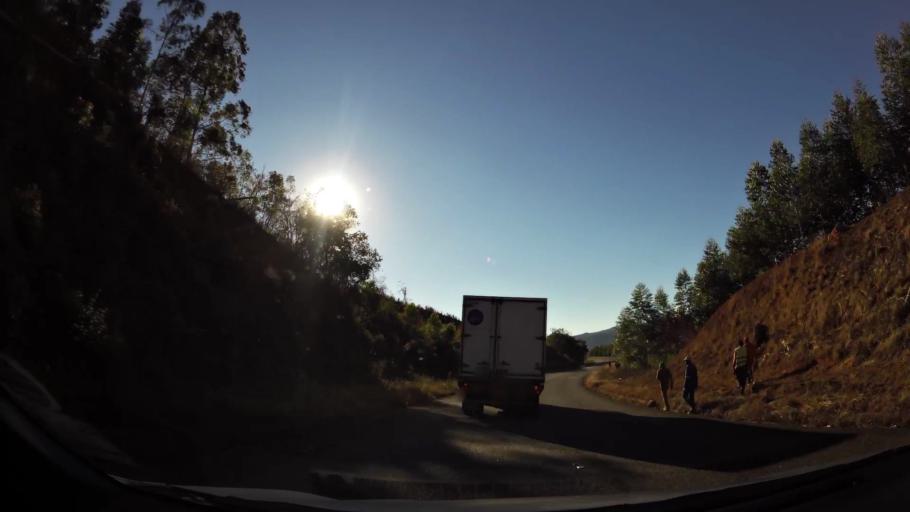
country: ZA
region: Limpopo
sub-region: Mopani District Municipality
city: Tzaneen
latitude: -23.9380
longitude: 30.0232
